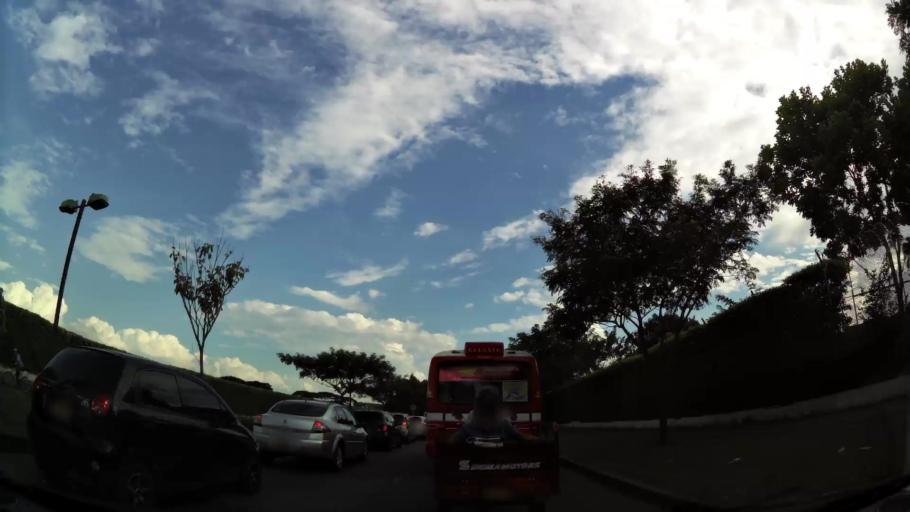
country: CO
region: Valle del Cauca
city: Cali
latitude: 3.4551
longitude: -76.5058
